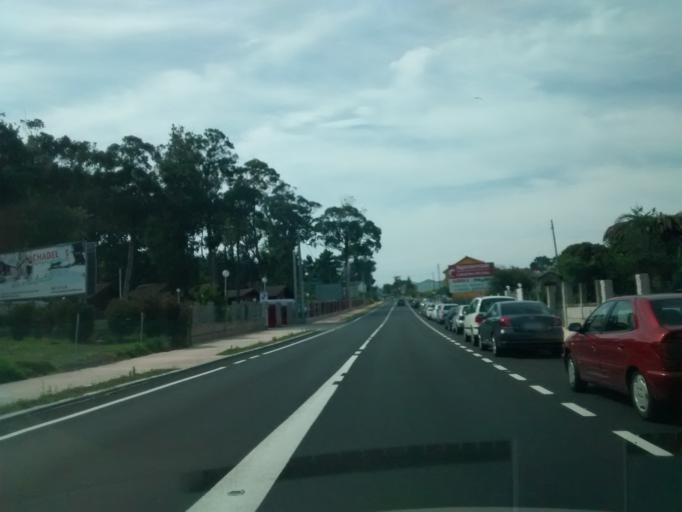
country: ES
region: Galicia
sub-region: Provincia de Pontevedra
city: Sanxenxo
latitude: 42.4172
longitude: -8.8688
